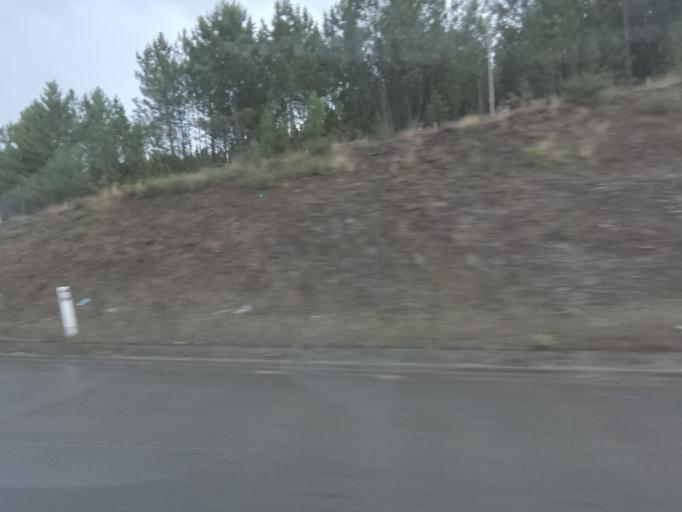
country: PT
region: Vila Real
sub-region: Vila Real
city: Vila Real
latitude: 41.2632
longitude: -7.7064
